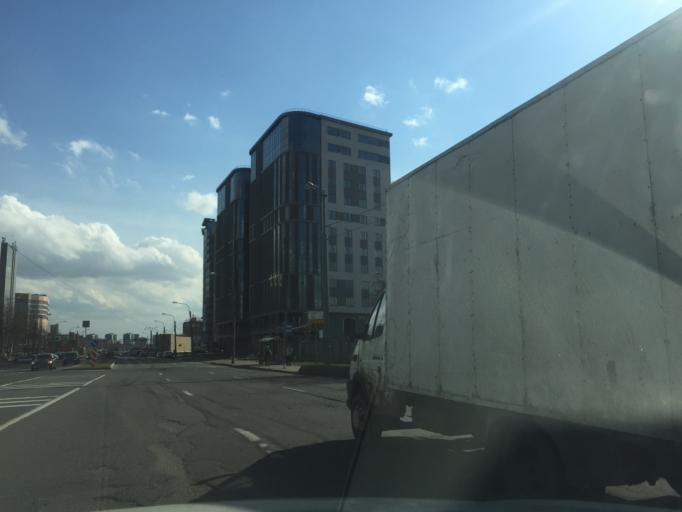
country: RU
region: St.-Petersburg
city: Krasnogvargeisky
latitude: 59.9366
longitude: 30.4352
